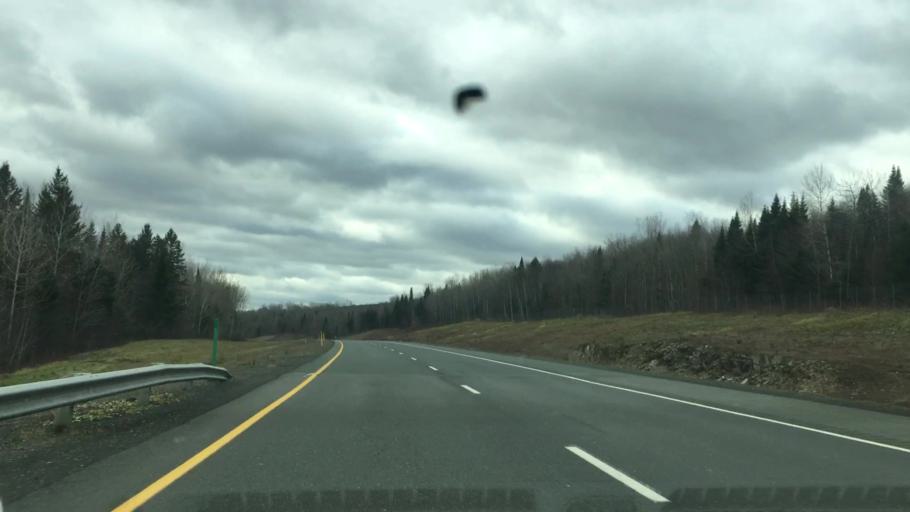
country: US
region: Maine
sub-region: Aroostook County
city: Fort Fairfield
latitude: 46.6521
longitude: -67.7399
